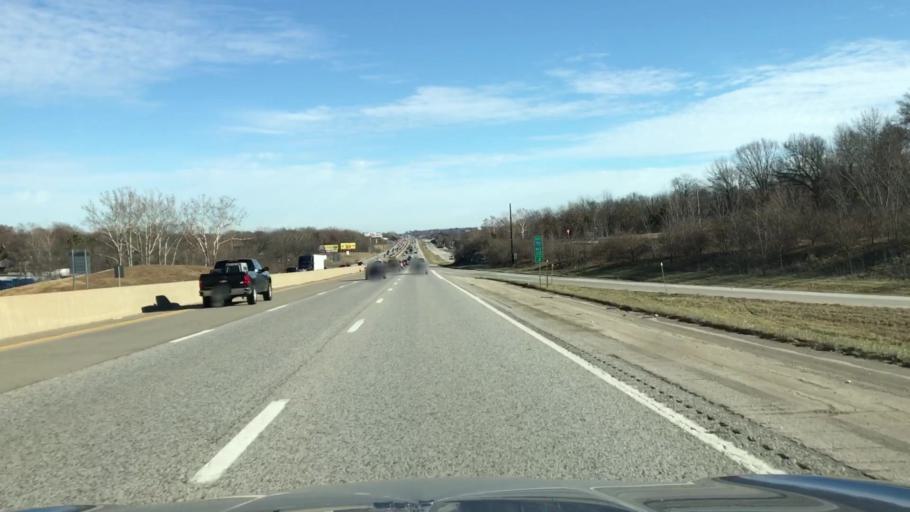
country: US
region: Missouri
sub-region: Saint Charles County
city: Lake Saint Louis
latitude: 38.8053
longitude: -90.8055
